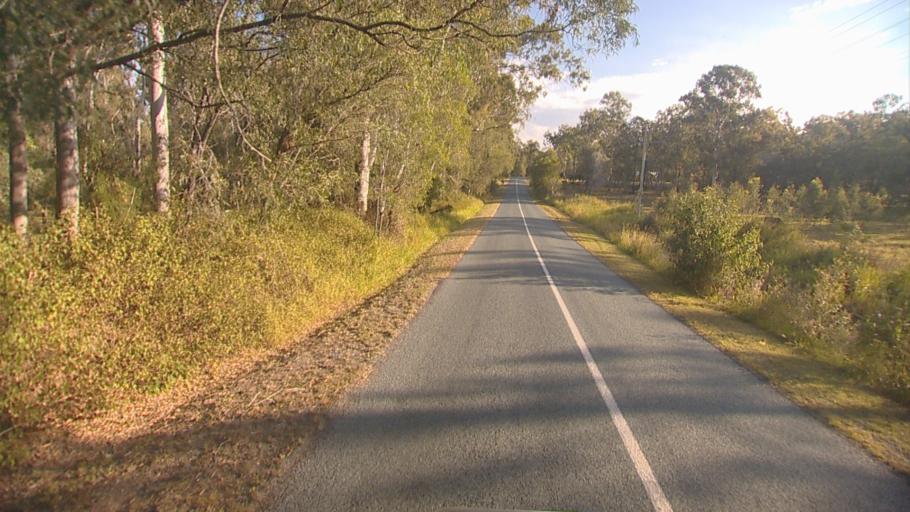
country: AU
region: Queensland
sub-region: Gold Coast
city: Ormeau Hills
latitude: -27.8401
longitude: 153.1645
